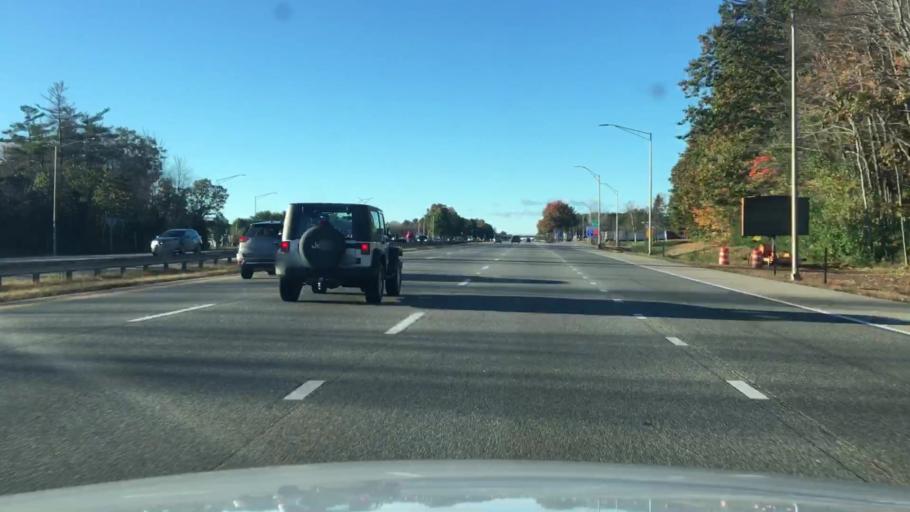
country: US
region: Maine
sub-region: York County
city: West Kennebunk
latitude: 43.4141
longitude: -70.5578
